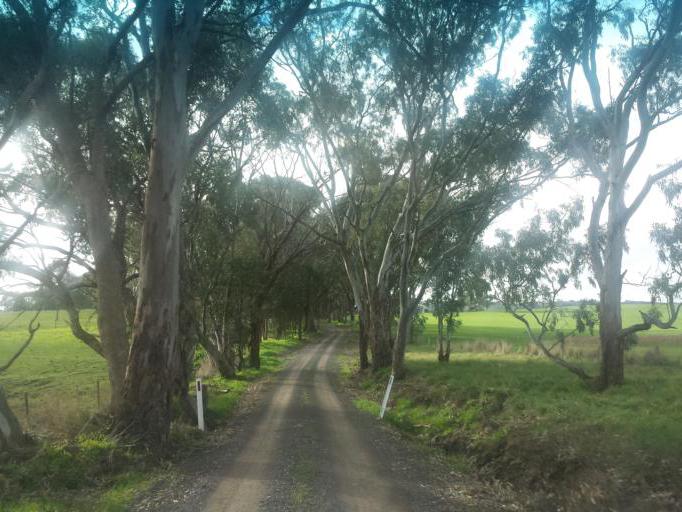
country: AU
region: Victoria
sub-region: Murrindindi
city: Kinglake West
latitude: -37.0285
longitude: 145.2501
